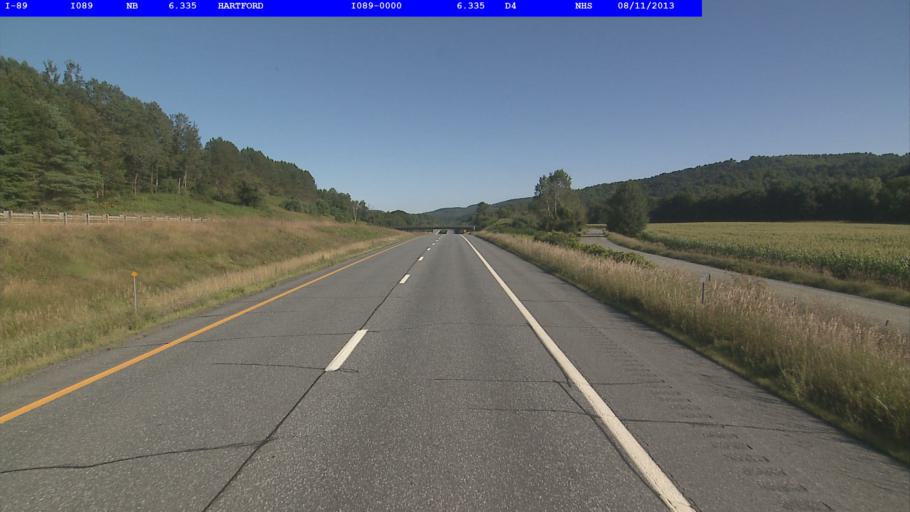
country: US
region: Vermont
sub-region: Windsor County
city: White River Junction
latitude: 43.6965
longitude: -72.4080
